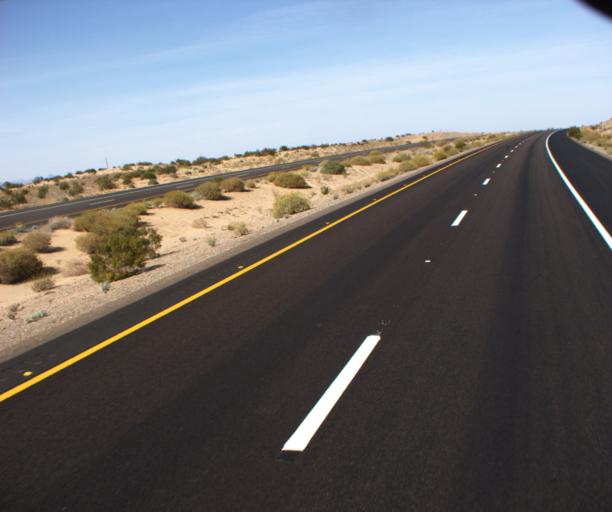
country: US
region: Arizona
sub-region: Yuma County
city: Somerton
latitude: 32.5595
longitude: -114.5614
